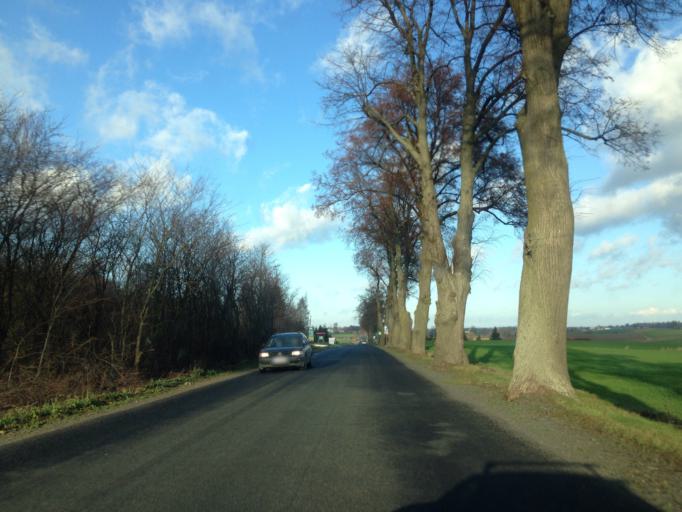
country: PL
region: Kujawsko-Pomorskie
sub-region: Powiat grudziadzki
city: Lasin
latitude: 53.5355
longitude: 19.0700
